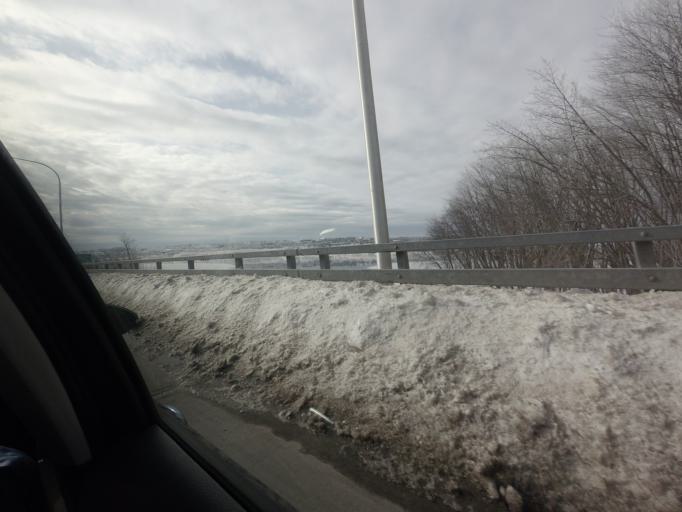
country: CA
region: New Brunswick
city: Fredericton
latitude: 45.9551
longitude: -66.6231
